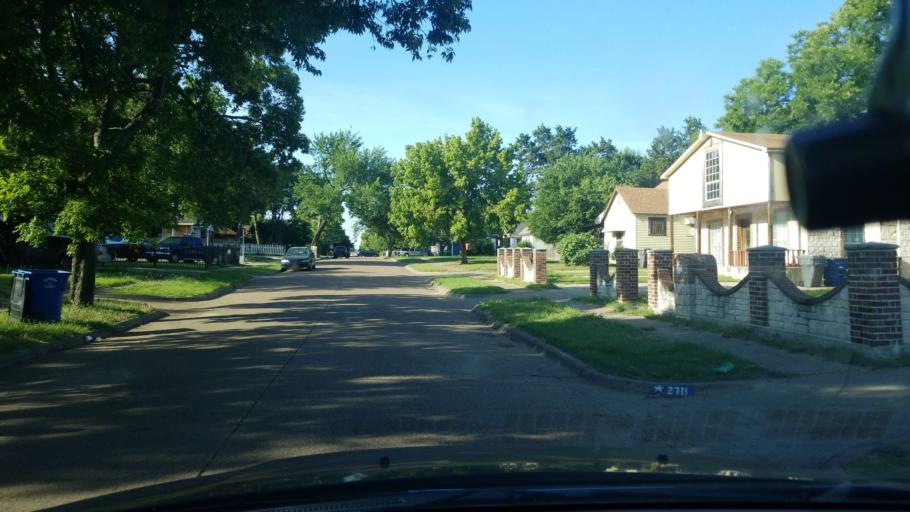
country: US
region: Texas
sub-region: Dallas County
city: Dallas
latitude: 32.7146
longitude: -96.8133
